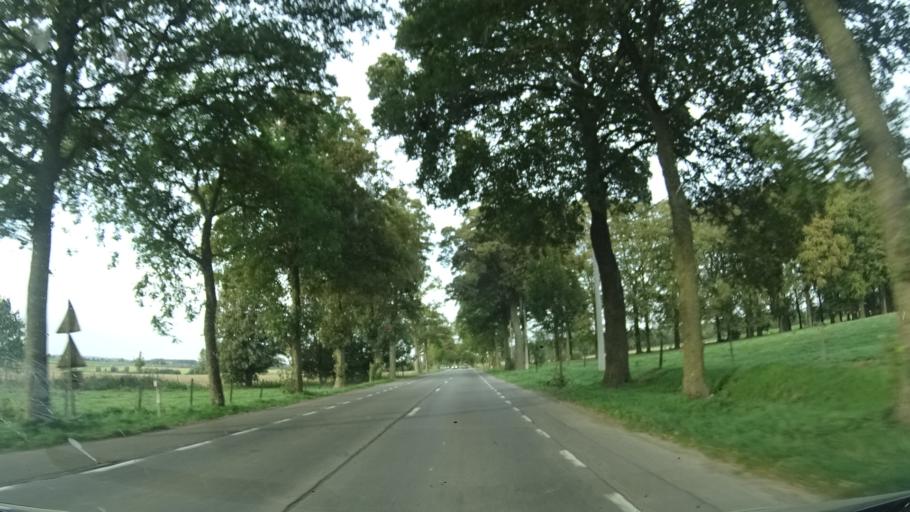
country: BE
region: Wallonia
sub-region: Province du Hainaut
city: Peruwelz
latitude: 50.5492
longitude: 3.6055
